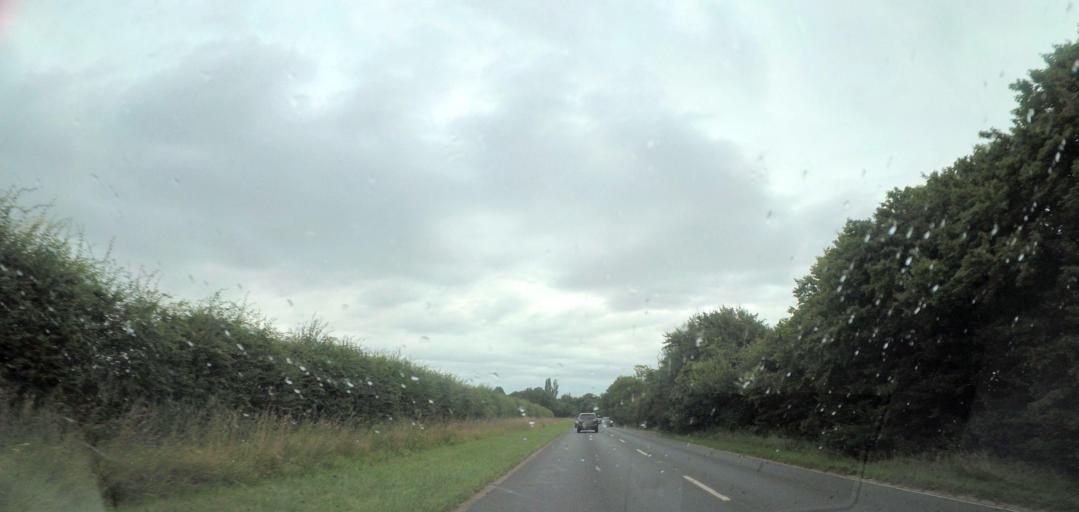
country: GB
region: England
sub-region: Norfolk
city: Coltishall
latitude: 52.7136
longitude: 1.3502
